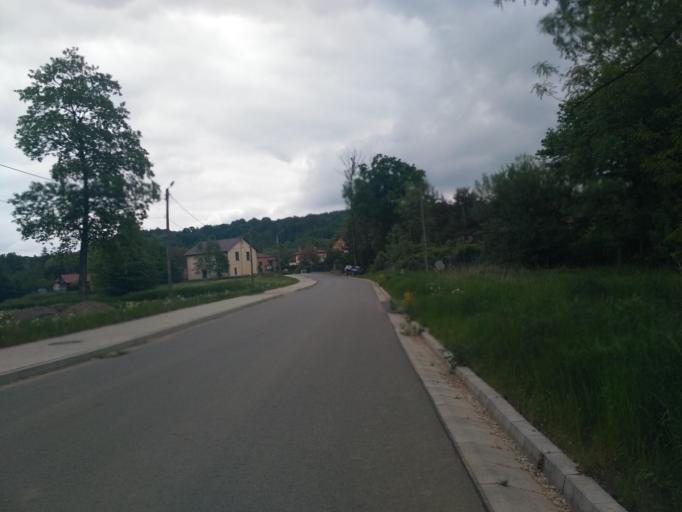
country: PL
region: Subcarpathian Voivodeship
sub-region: Powiat krosnienski
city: Wojaszowka
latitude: 49.7727
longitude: 21.6864
